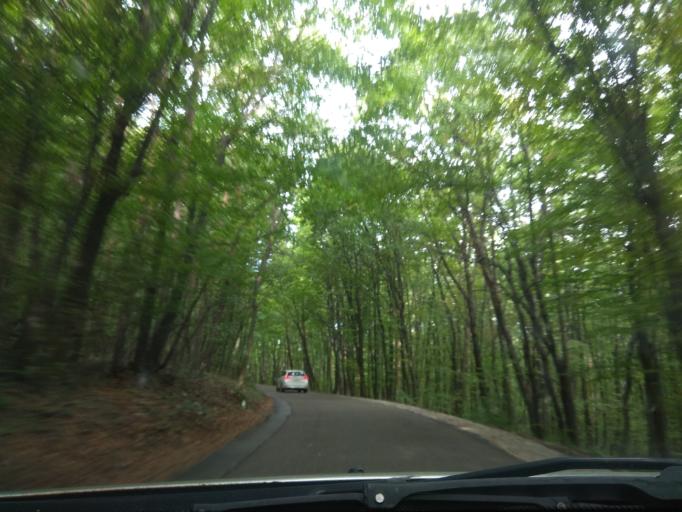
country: HU
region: Borsod-Abauj-Zemplen
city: Sajobabony
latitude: 48.0693
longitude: 20.6694
